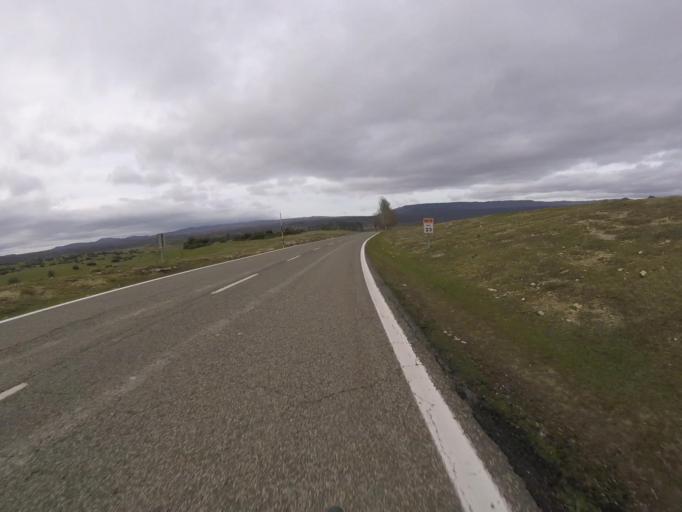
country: ES
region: Navarre
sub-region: Provincia de Navarra
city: Eulate
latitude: 42.8049
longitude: -2.1506
